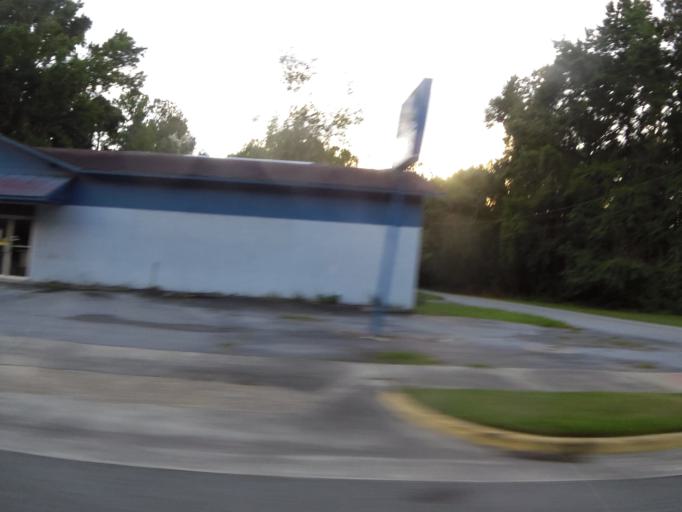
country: US
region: Georgia
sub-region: Camden County
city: Woodbine
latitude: 30.9651
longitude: -81.7232
